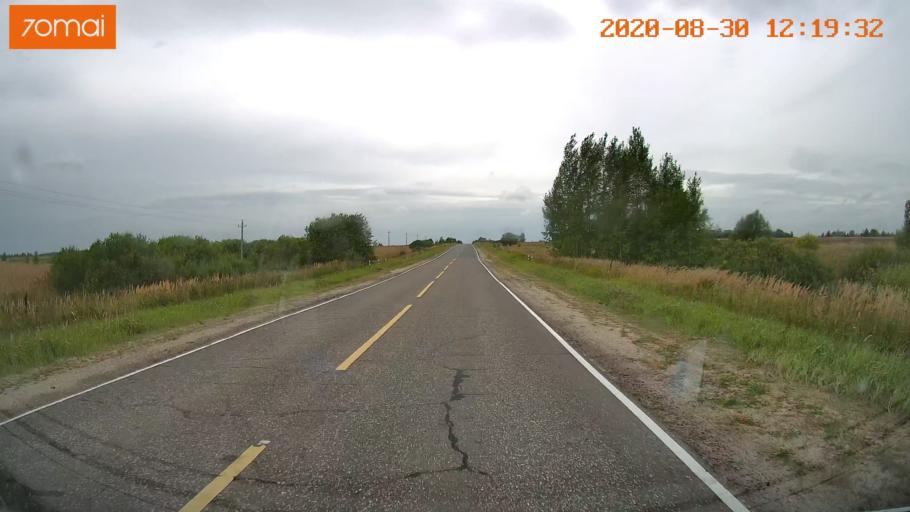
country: RU
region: Ivanovo
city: Yur'yevets
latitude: 57.3230
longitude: 42.9249
